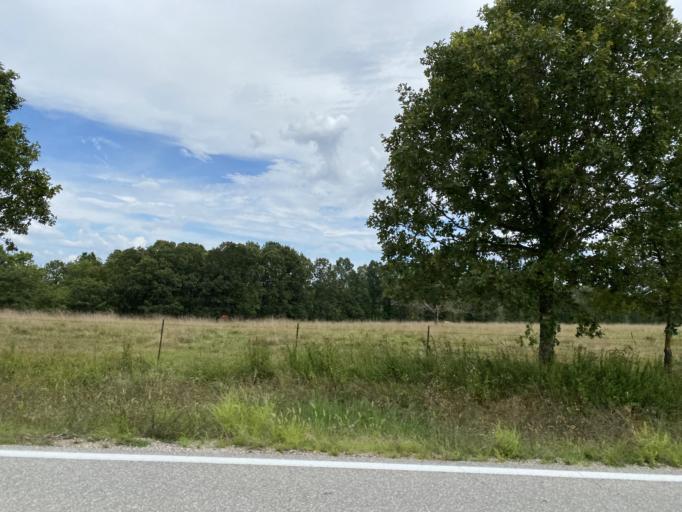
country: US
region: Arkansas
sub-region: Fulton County
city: Salem
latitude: 36.4246
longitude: -91.7091
